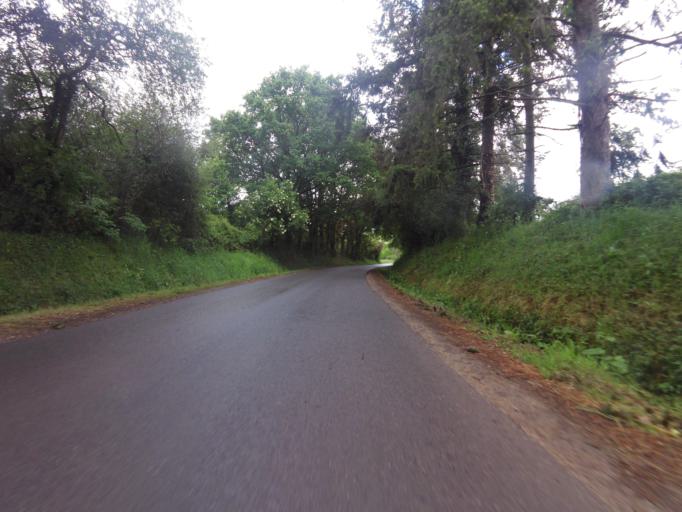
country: FR
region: Brittany
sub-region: Departement du Morbihan
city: Plougoumelen
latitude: 47.6452
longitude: -2.8959
